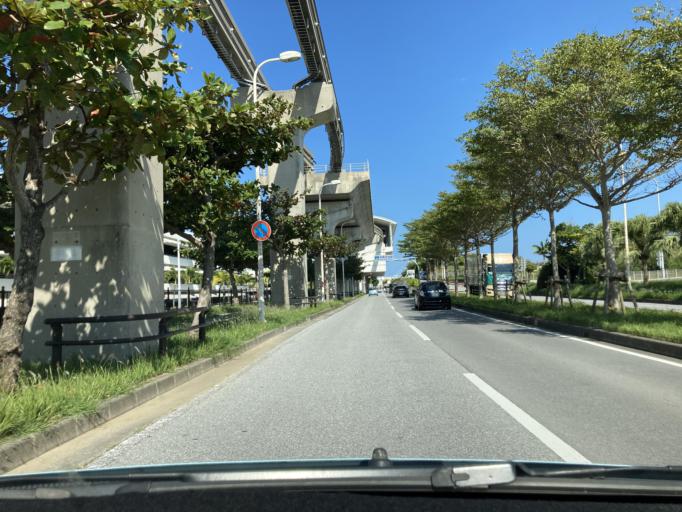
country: JP
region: Okinawa
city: Naha-shi
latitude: 26.2050
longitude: 127.6524
